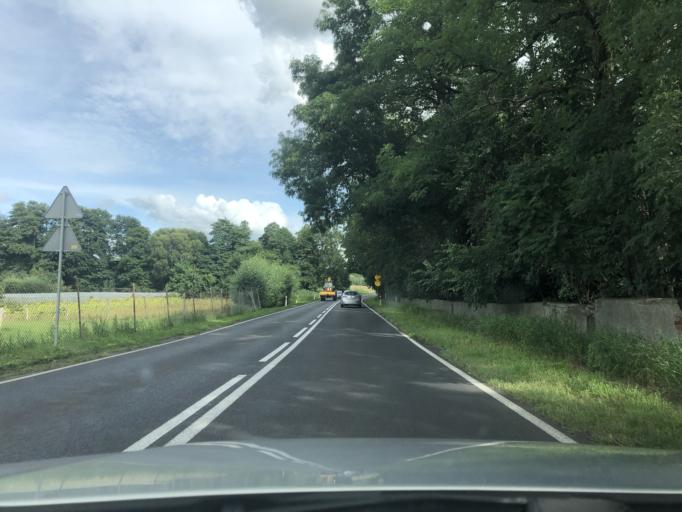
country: PL
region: Greater Poland Voivodeship
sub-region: Powiat pilski
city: Szydlowo
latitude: 53.0789
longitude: 16.5982
